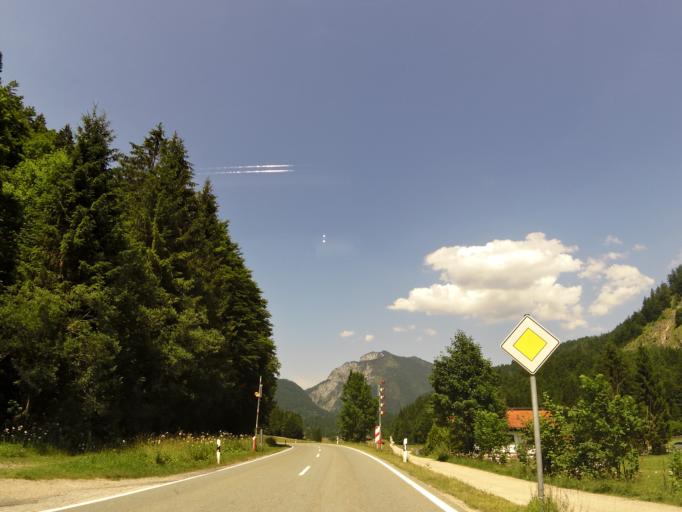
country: DE
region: Bavaria
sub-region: Upper Bavaria
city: Reit im Winkl
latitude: 47.6614
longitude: 12.5423
